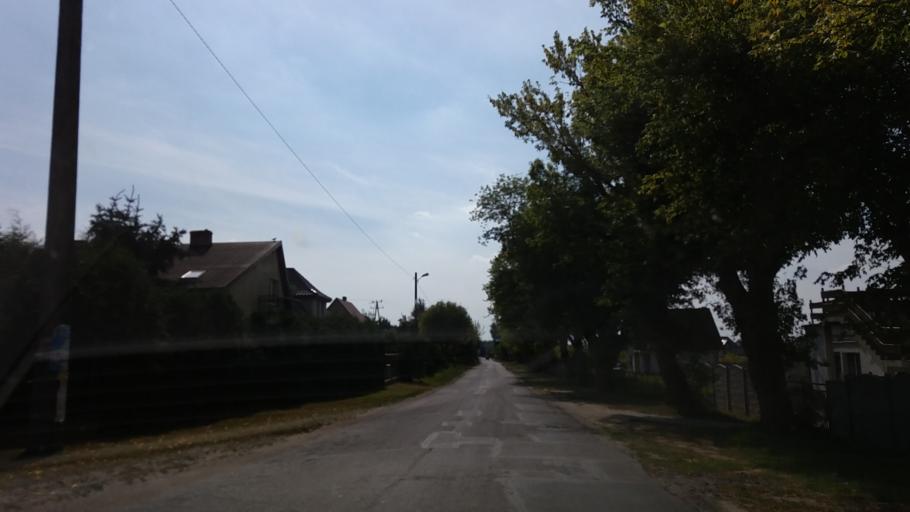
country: PL
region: West Pomeranian Voivodeship
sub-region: Powiat stargardzki
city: Stargard Szczecinski
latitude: 53.3664
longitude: 14.9727
